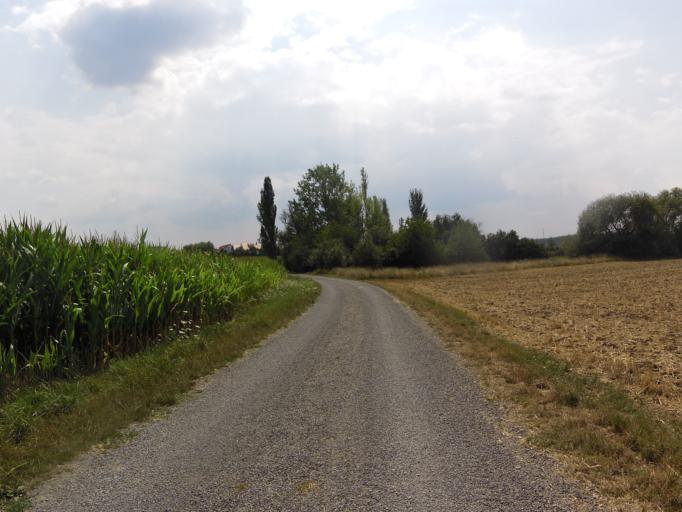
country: DE
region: Bavaria
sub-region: Regierungsbezirk Unterfranken
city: Eibelstadt
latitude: 49.7296
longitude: 9.9696
